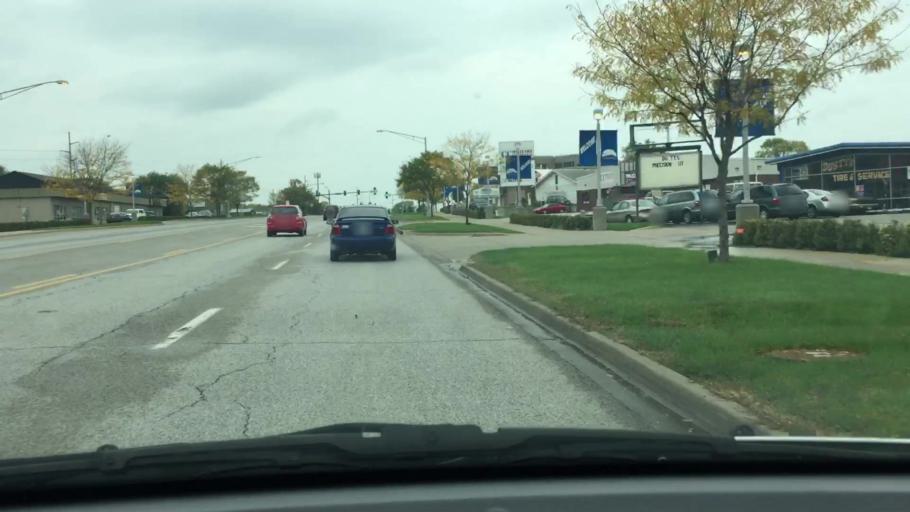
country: US
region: Iowa
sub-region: Johnson County
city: Coralville
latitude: 41.6721
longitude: -91.5758
